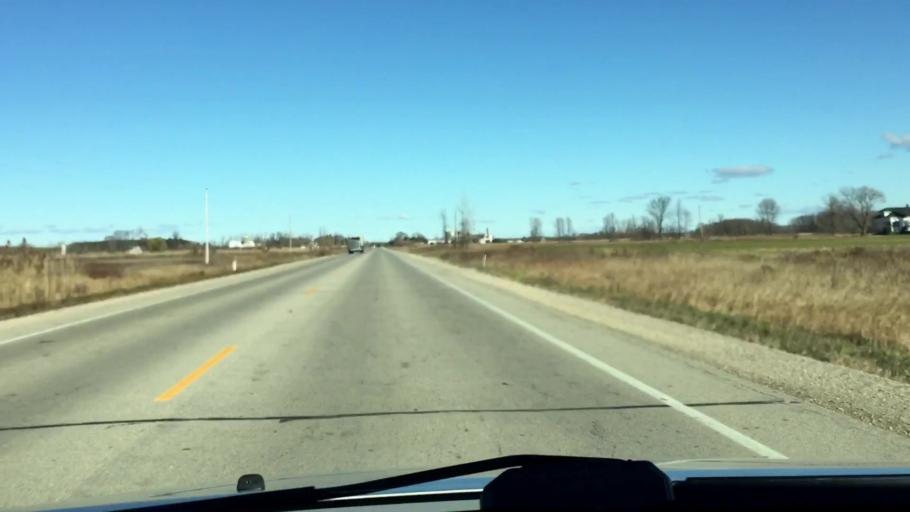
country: US
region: Wisconsin
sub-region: Brown County
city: Pulaski
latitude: 44.7205
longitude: -88.2459
